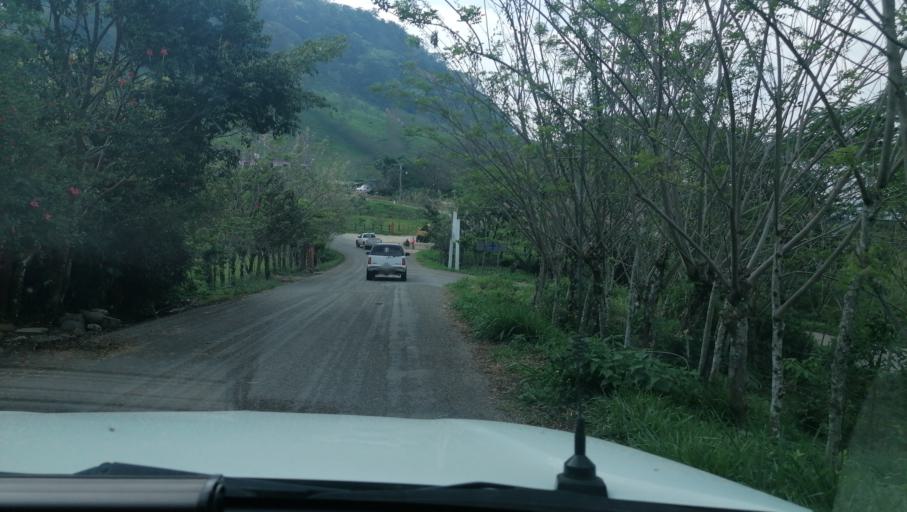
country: MX
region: Chiapas
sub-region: Francisco Leon
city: San Miguel la Sardina
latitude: 17.2303
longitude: -93.3524
